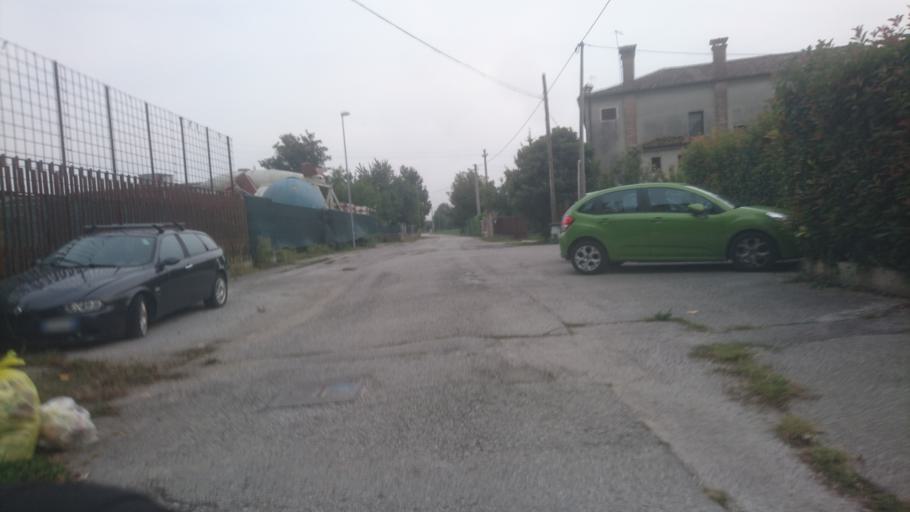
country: IT
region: Veneto
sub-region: Provincia di Padova
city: Selvazzano Dentro
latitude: 45.3952
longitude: 11.7744
